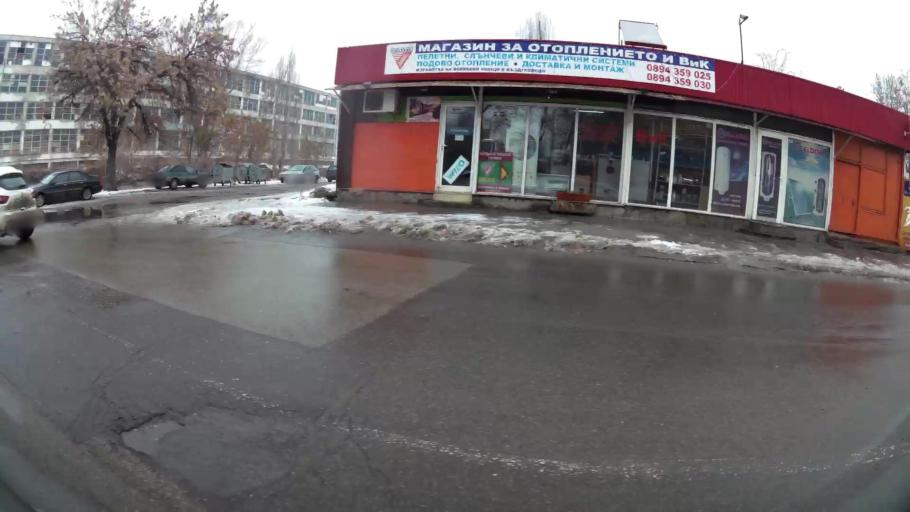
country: BG
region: Sofia-Capital
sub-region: Stolichna Obshtina
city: Sofia
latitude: 42.7073
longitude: 23.3363
